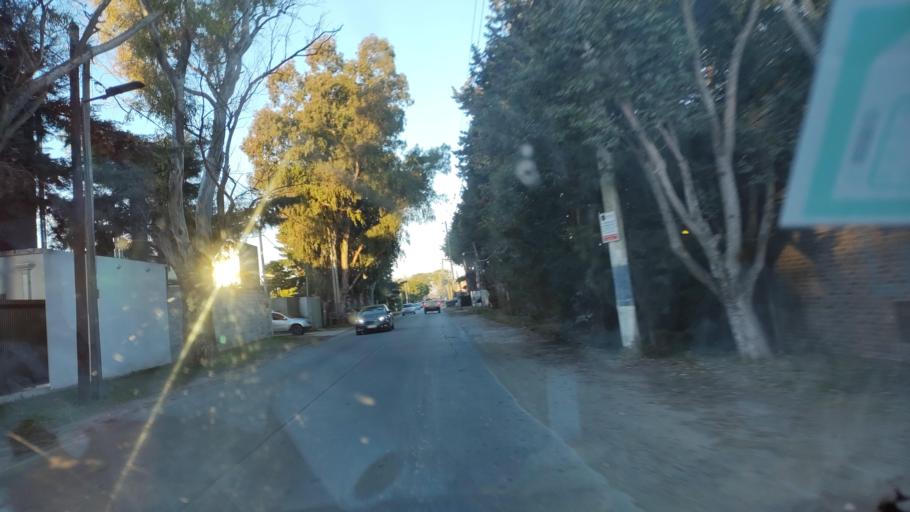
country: AR
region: Buenos Aires
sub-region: Partido de La Plata
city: La Plata
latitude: -34.8999
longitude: -58.0364
